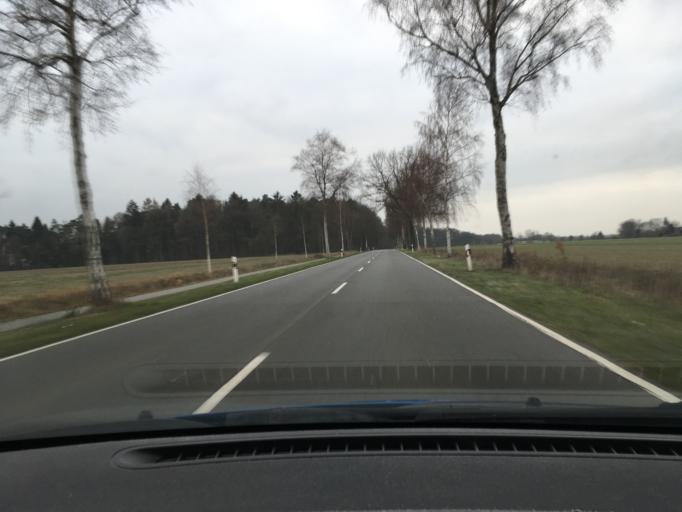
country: DE
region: Lower Saxony
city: Bad Fallingbostel
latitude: 52.8773
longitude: 9.7171
